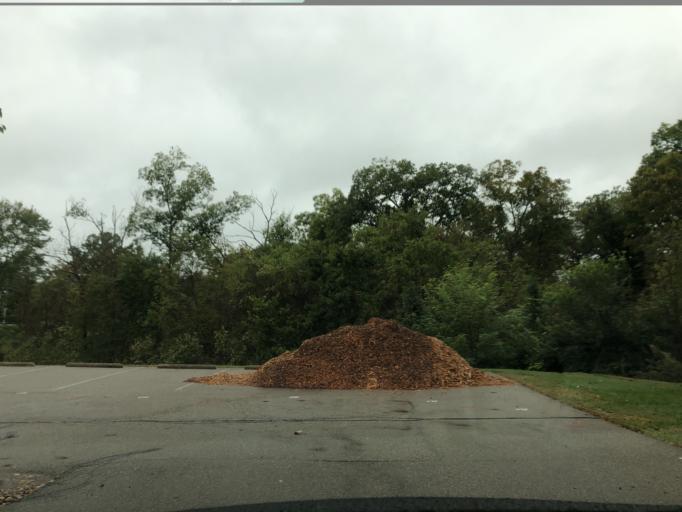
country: US
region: Ohio
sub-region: Hamilton County
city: Loveland
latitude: 39.2597
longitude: -84.2478
